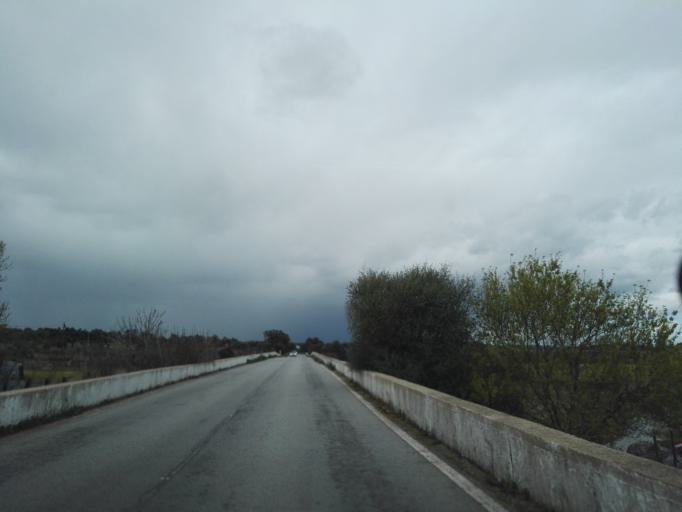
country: PT
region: Portalegre
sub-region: Arronches
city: Arronches
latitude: 38.9931
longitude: -7.2423
